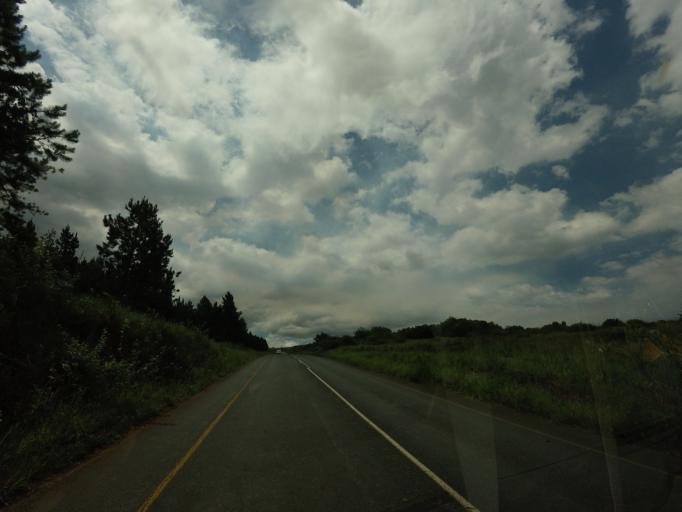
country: ZA
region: Mpumalanga
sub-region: Ehlanzeni District
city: Graksop
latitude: -24.9566
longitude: 30.8120
